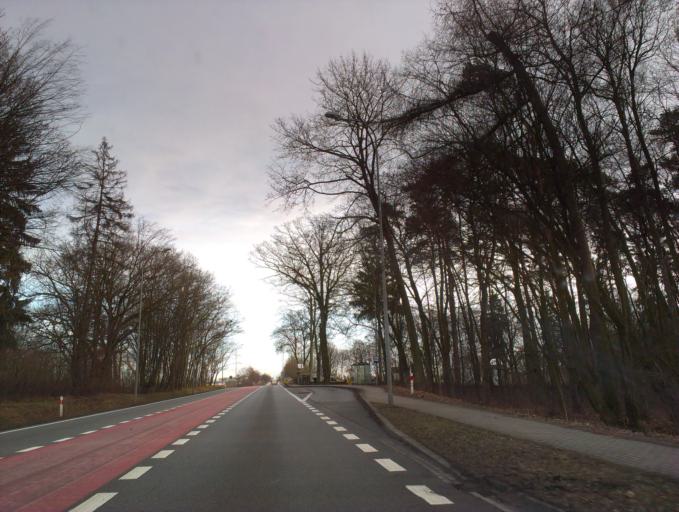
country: PL
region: Kujawsko-Pomorskie
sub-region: Powiat lipnowski
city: Lipno
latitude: 52.8578
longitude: 19.2525
